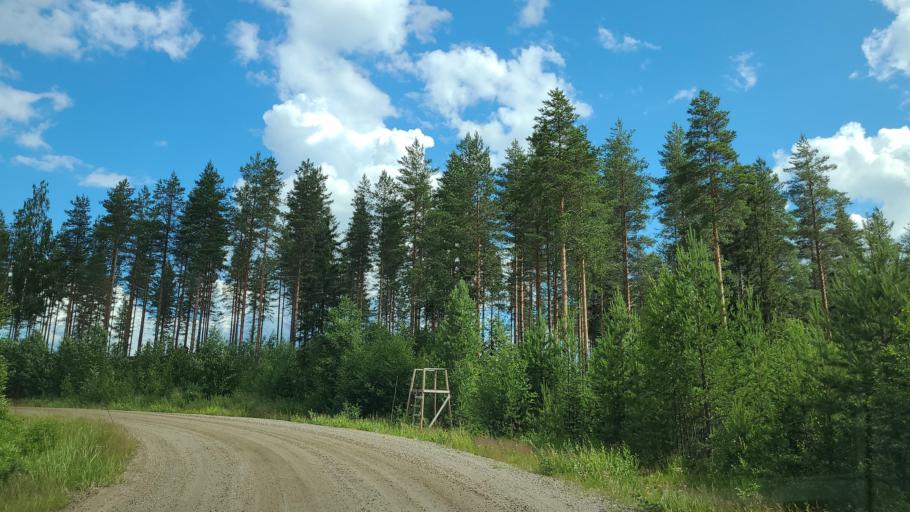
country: FI
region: Northern Savo
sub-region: Koillis-Savo
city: Kaavi
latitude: 63.0298
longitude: 28.7856
